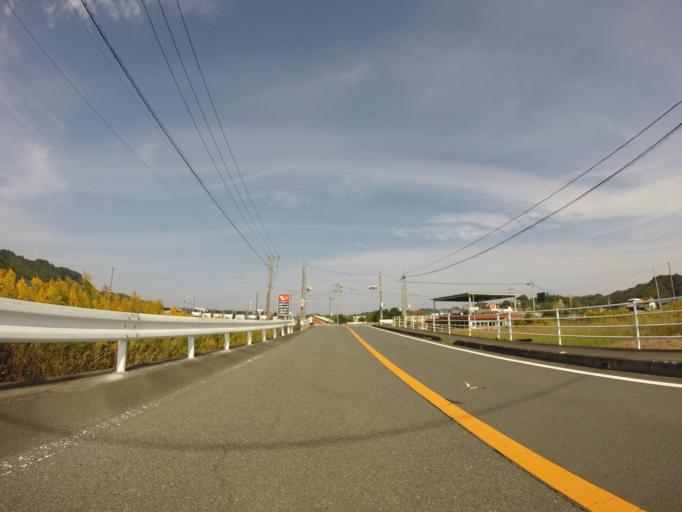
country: JP
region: Shizuoka
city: Shimada
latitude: 34.7642
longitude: 138.1876
